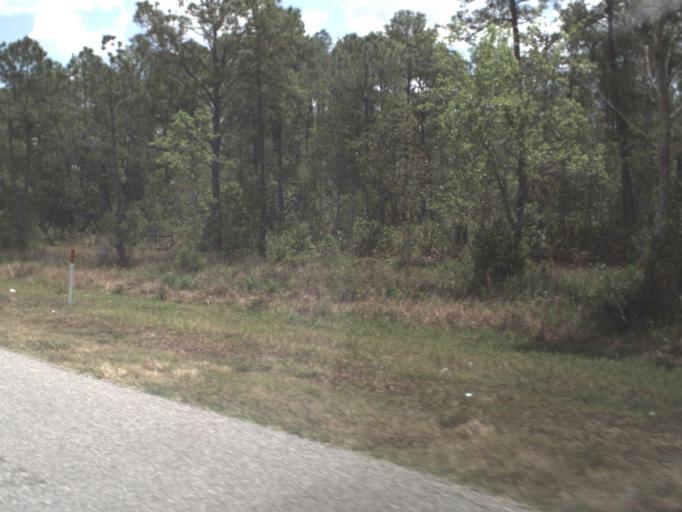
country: US
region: Florida
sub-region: Orange County
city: Alafaya
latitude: 28.4515
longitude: -81.1915
